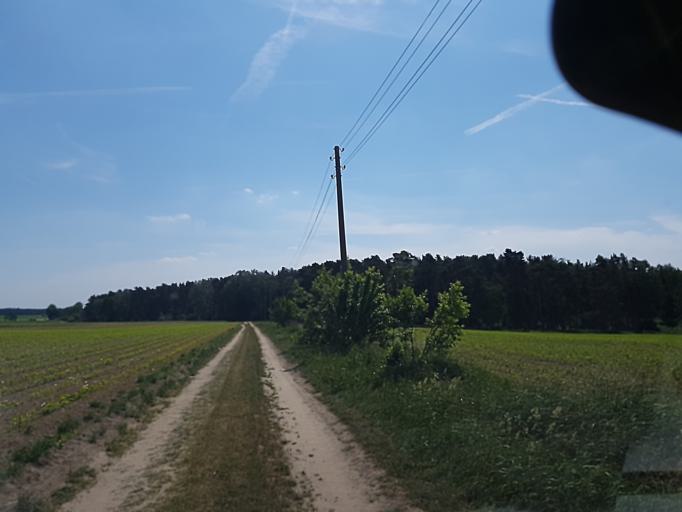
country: DE
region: Brandenburg
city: Gorzke
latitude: 52.0988
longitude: 12.3508
